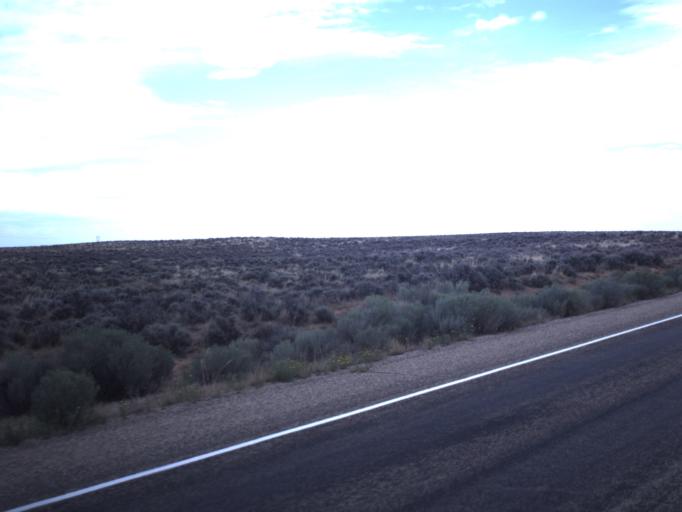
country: US
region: Utah
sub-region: Uintah County
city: Naples
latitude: 40.1569
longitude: -109.3065
